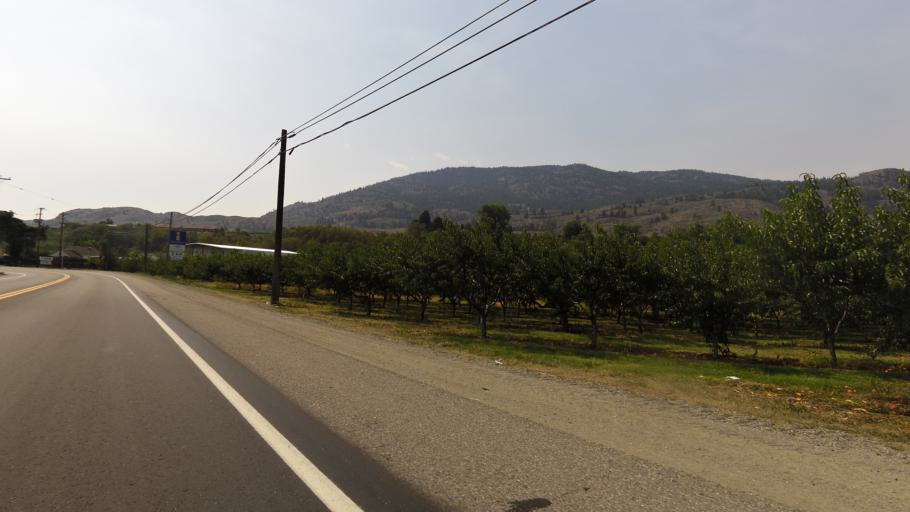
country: CA
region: British Columbia
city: Osoyoos
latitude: 49.0489
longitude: -119.4981
